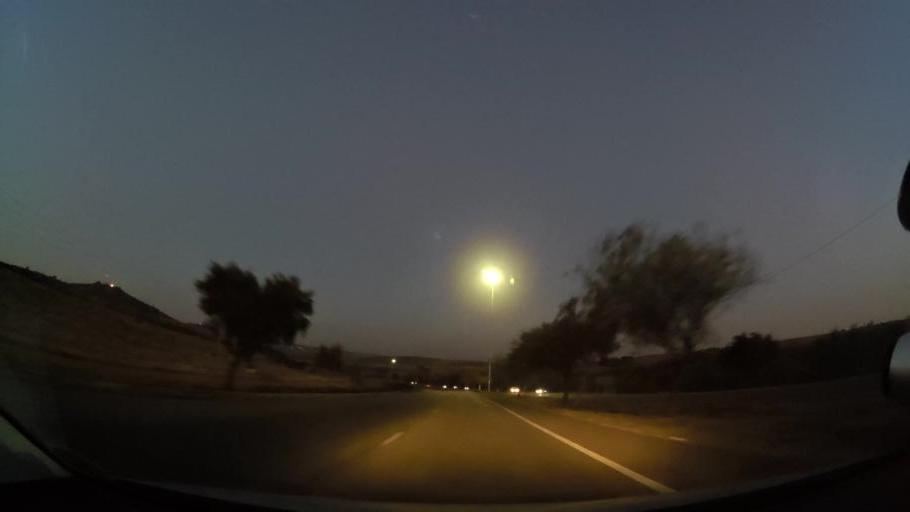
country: ZA
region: Gauteng
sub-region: City of Tshwane Metropolitan Municipality
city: Pretoria
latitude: -25.7799
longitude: 28.1716
